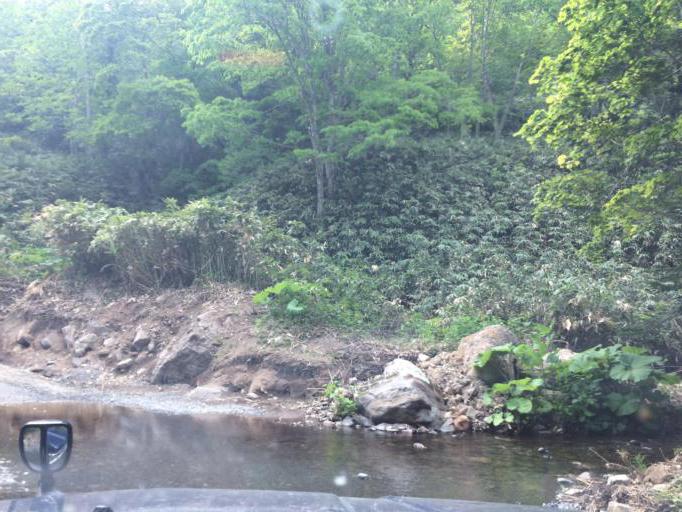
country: JP
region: Hokkaido
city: Niseko Town
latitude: 42.6544
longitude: 140.5052
